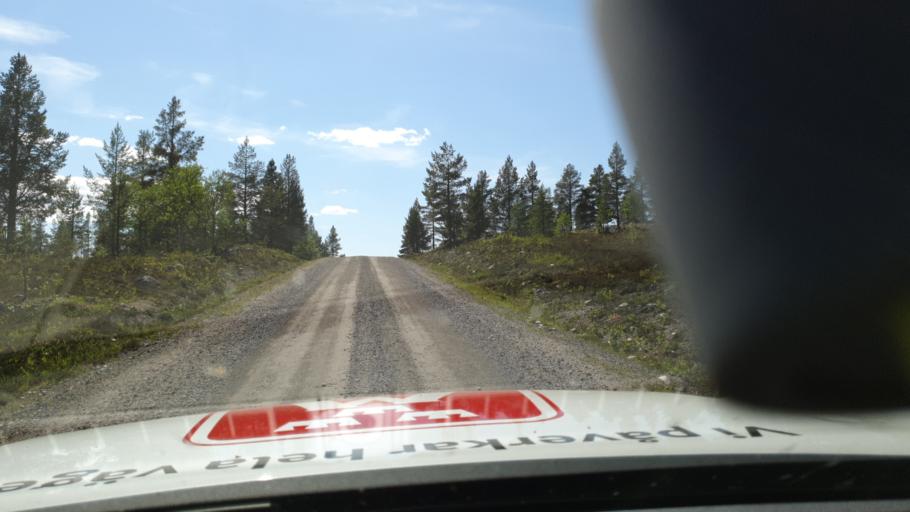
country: NO
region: Hedmark
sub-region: Engerdal
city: Engerdal
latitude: 62.1332
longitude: 12.9207
